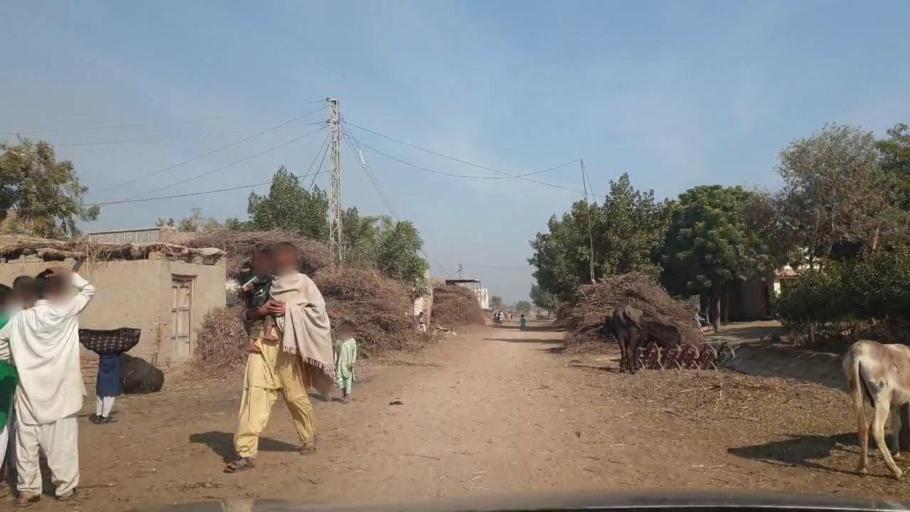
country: PK
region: Sindh
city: Tando Allahyar
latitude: 25.6020
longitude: 68.7222
